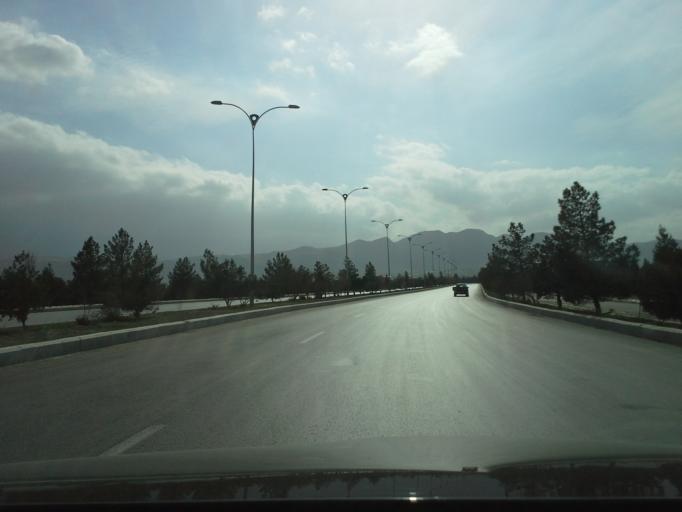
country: TM
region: Ahal
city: Abadan
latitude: 37.9742
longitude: 58.2423
